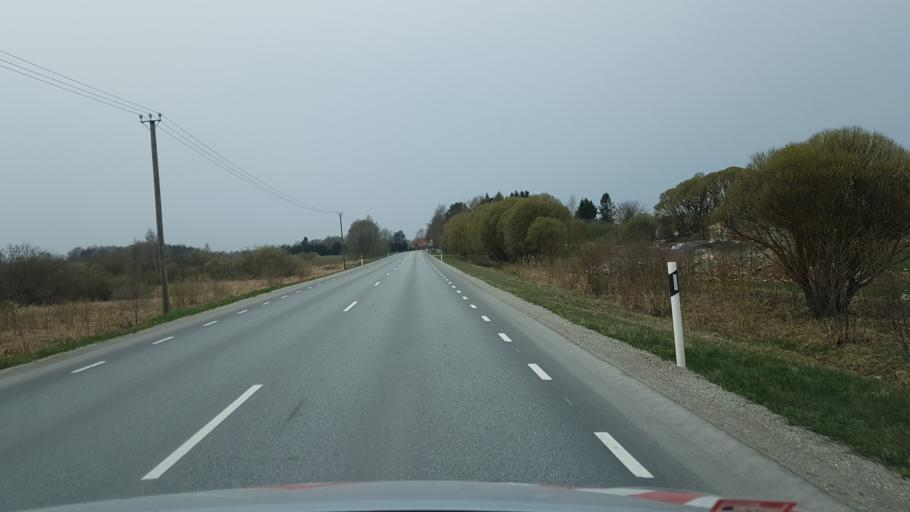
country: EE
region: Harju
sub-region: Joelaehtme vald
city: Loo
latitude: 59.3926
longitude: 24.9729
